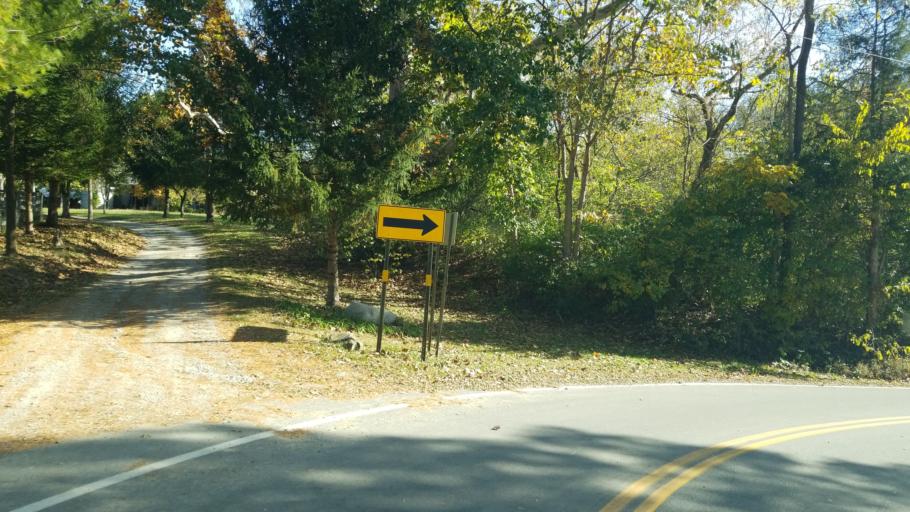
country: US
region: Ohio
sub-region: Warren County
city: Morrow
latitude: 39.3785
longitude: -84.0957
